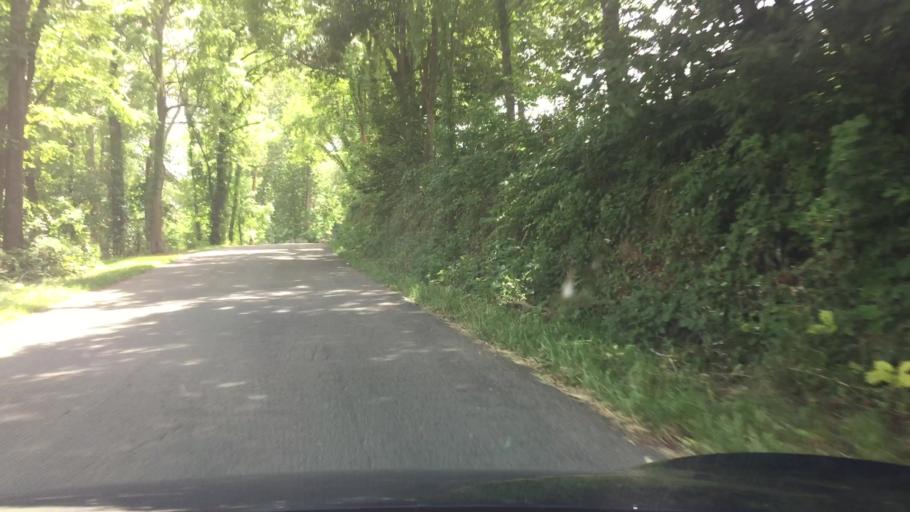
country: US
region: Virginia
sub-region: Wythe County
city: Wytheville
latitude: 36.9340
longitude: -81.0279
